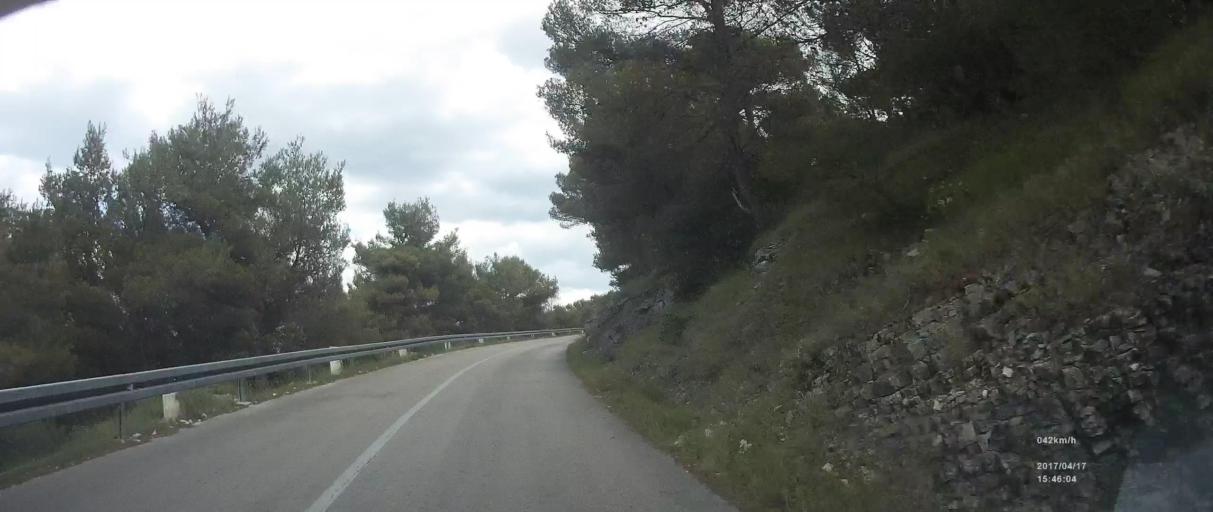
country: HR
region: Sibensko-Kniniska
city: Primosten
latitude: 43.6264
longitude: 15.9678
